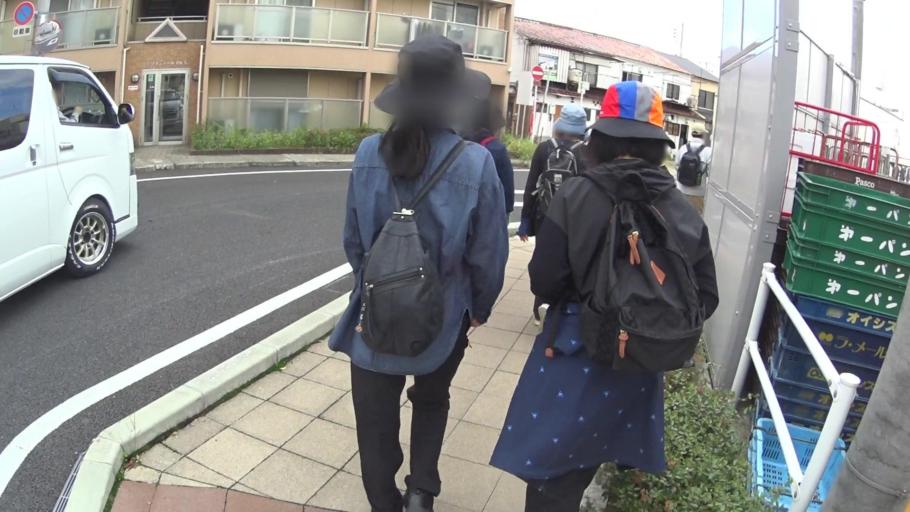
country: JP
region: Osaka
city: Kashihara
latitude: 34.5739
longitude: 135.5918
